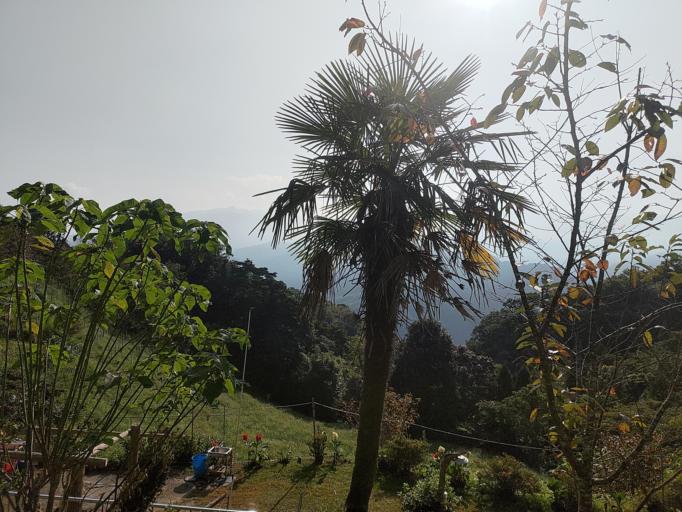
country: TW
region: Taiwan
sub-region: Hsinchu
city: Hsinchu
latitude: 24.6210
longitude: 121.0906
